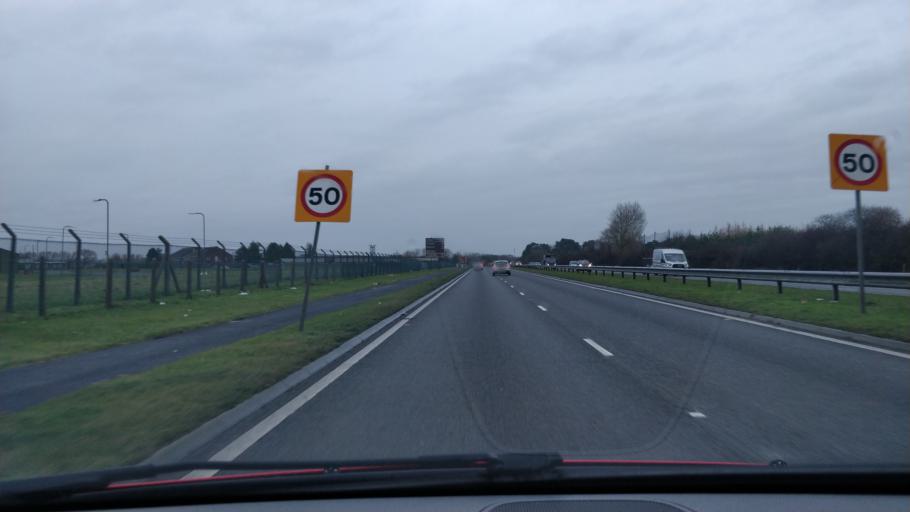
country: GB
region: England
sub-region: Sefton
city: Formby
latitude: 53.5814
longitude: -3.0480
